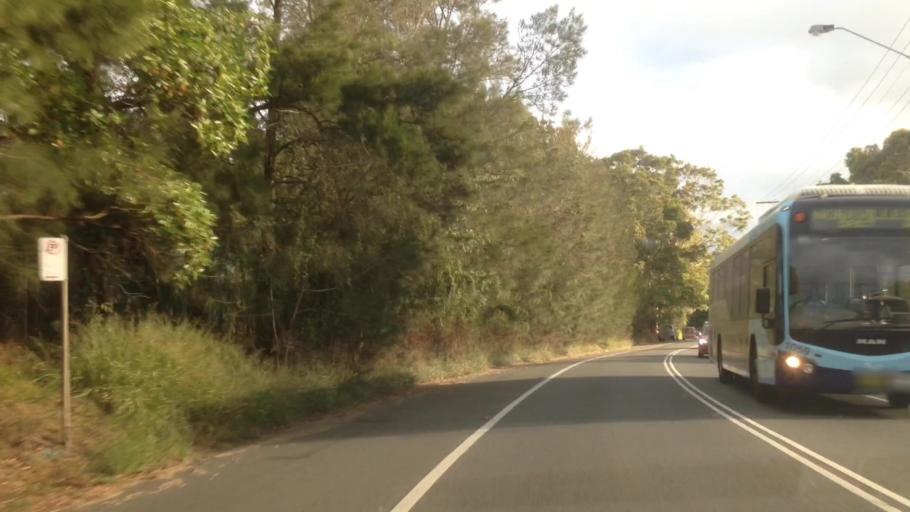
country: AU
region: New South Wales
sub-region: Wyong Shire
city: Chittaway Bay
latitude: -33.2870
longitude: 151.4244
